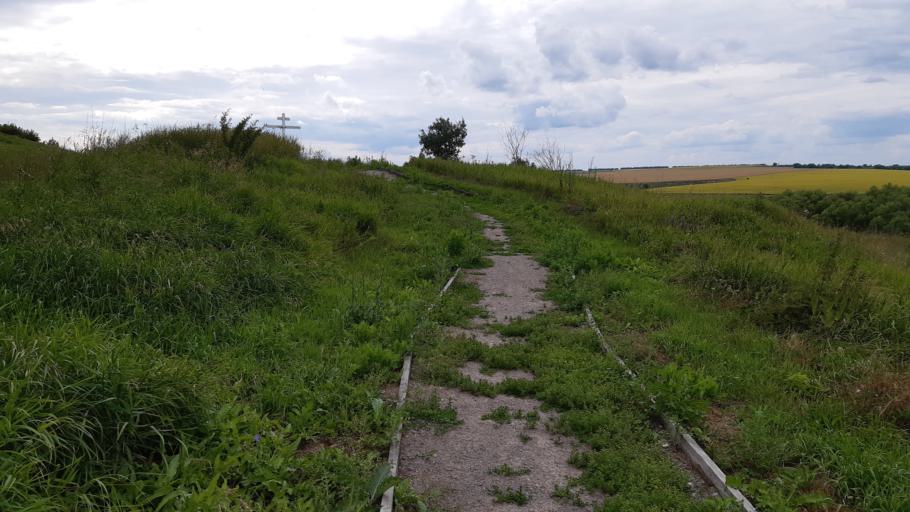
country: RU
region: Tula
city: Yepifan'
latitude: 53.6696
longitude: 38.6525
